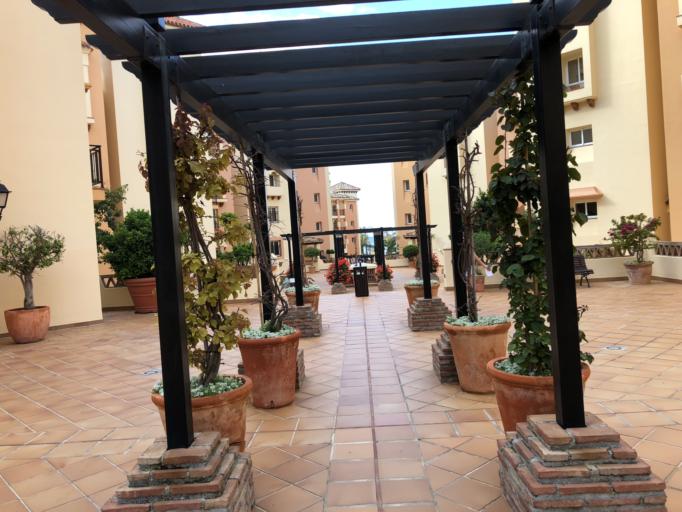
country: ES
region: Andalusia
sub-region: Provincia de Malaga
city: Ojen
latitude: 36.4905
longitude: -4.7707
